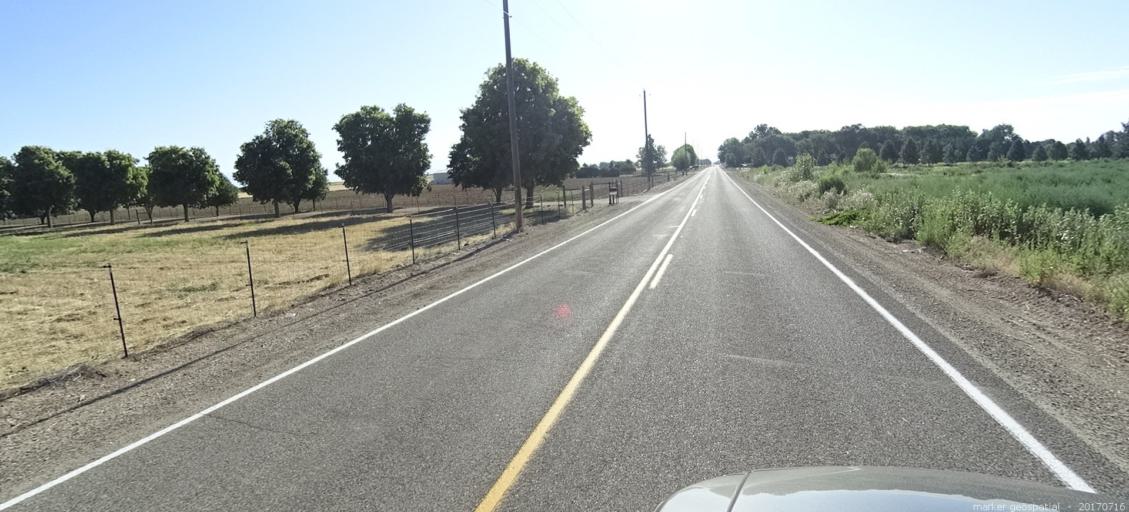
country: US
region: Idaho
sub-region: Ada County
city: Kuna
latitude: 43.5465
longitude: -116.4059
